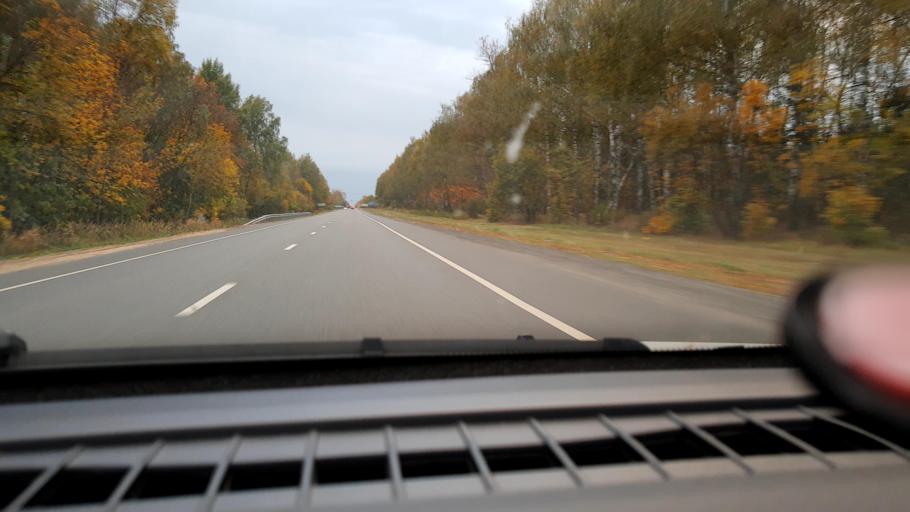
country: RU
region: Vladimir
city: Kameshkovo
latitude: 56.1975
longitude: 40.8595
